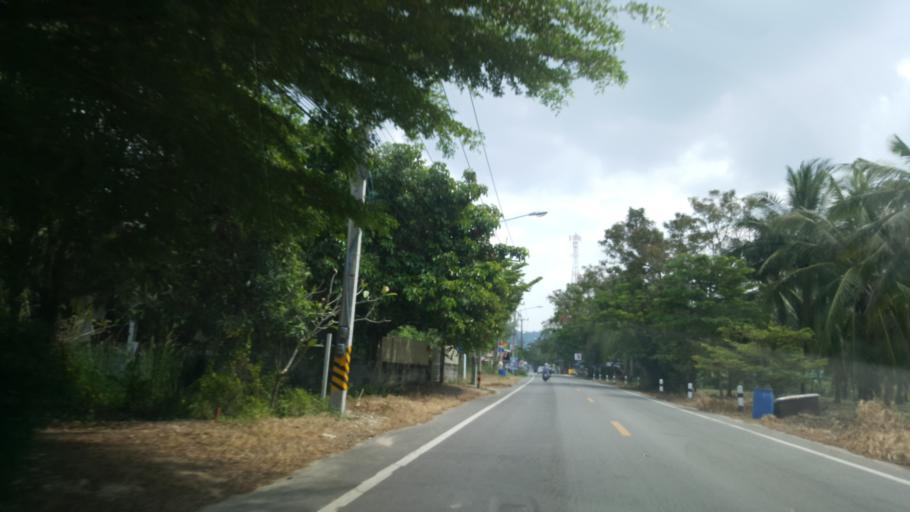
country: TH
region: Chon Buri
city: Si Racha
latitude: 13.2100
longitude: 101.0327
